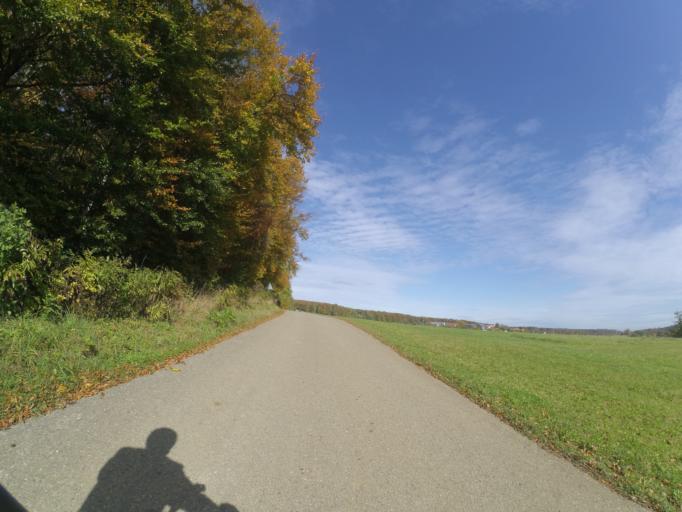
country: DE
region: Baden-Wuerttemberg
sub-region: Tuebingen Region
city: Weidenstetten
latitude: 48.5832
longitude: 9.9835
